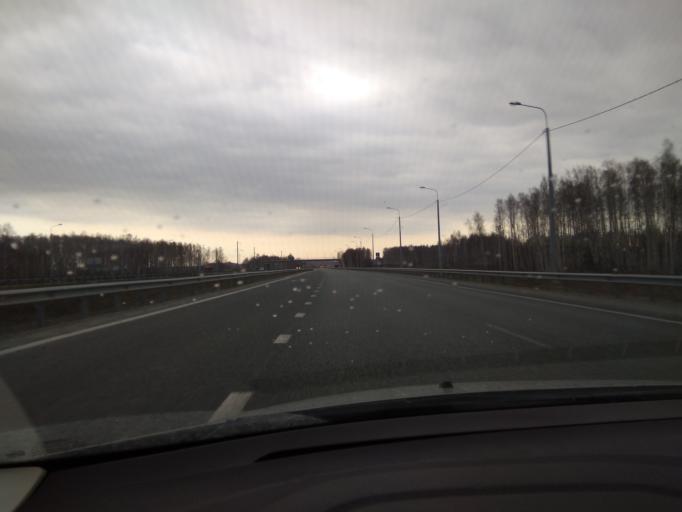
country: RU
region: Chelyabinsk
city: Kunashak
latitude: 55.7651
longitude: 61.2194
